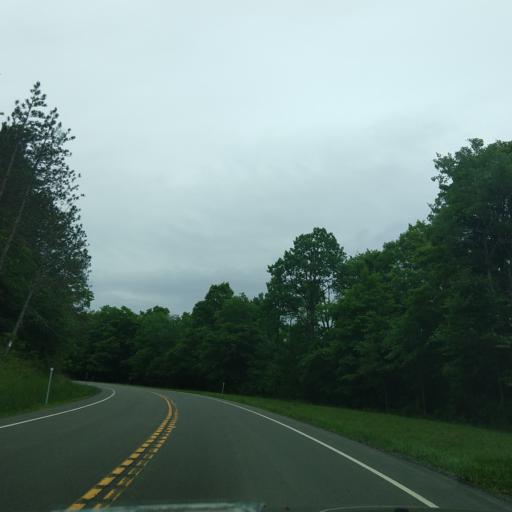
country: US
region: New York
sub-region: Cortland County
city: McGraw
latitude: 42.4872
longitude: -76.0847
